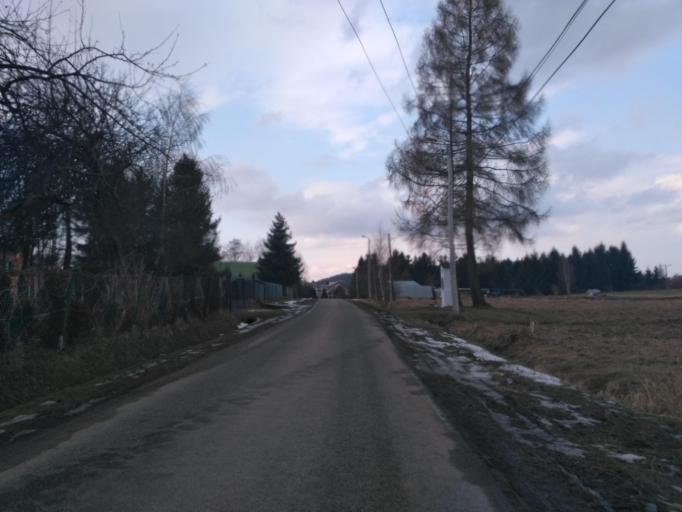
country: PL
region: Subcarpathian Voivodeship
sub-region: Powiat sanocki
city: Strachocina
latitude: 49.6111
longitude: 22.0788
